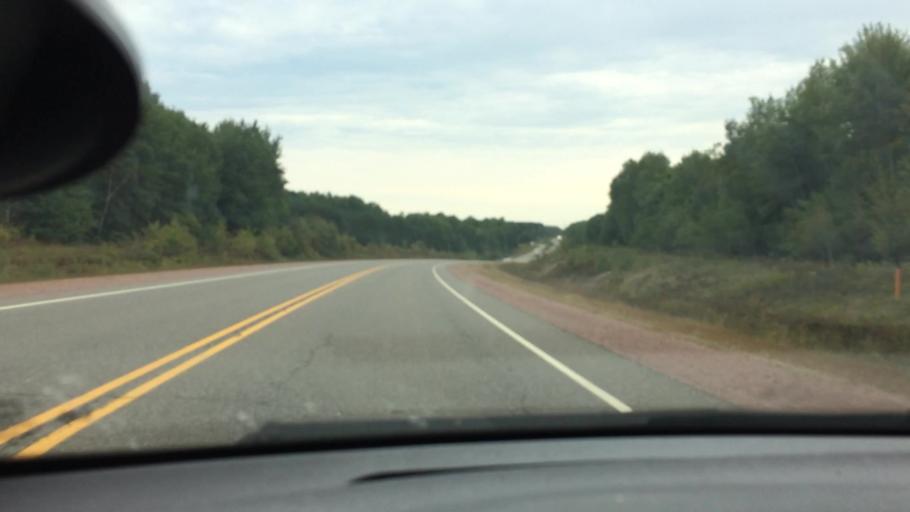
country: US
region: Wisconsin
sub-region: Clark County
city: Neillsville
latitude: 44.5681
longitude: -90.7236
